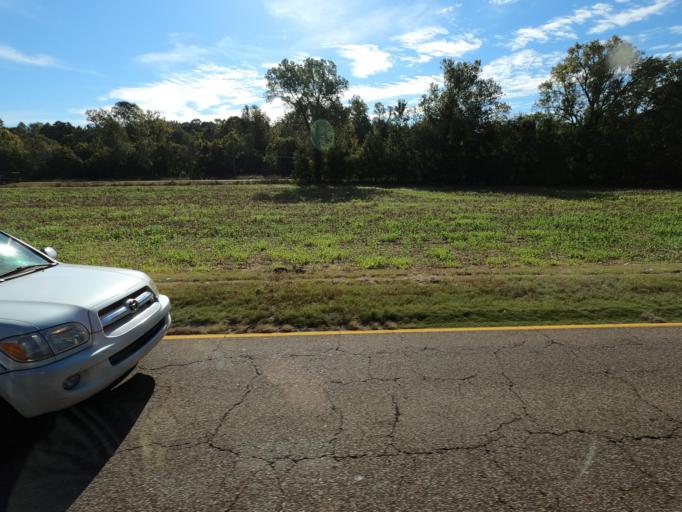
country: US
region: Tennessee
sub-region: Tipton County
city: Brighton
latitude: 35.5147
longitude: -89.7066
